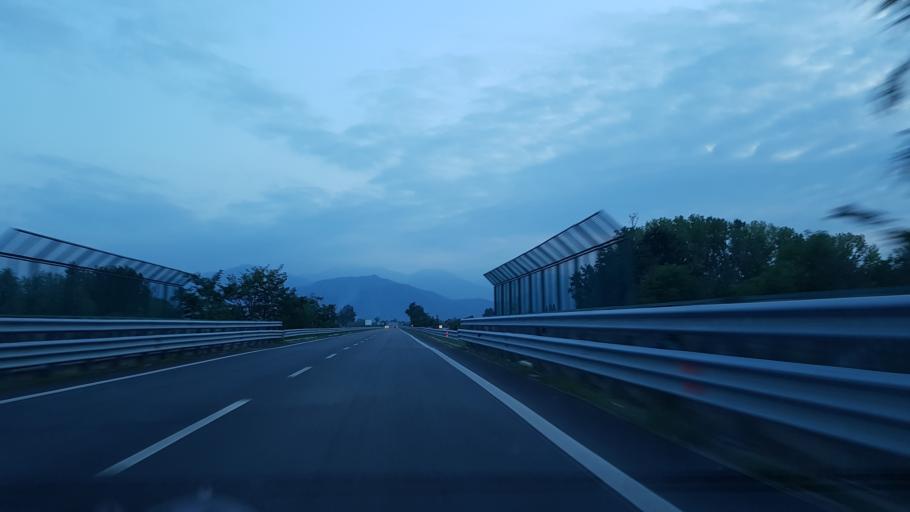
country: IT
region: Piedmont
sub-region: Provincia di Cuneo
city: Mondovi
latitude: 44.3851
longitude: 7.7930
